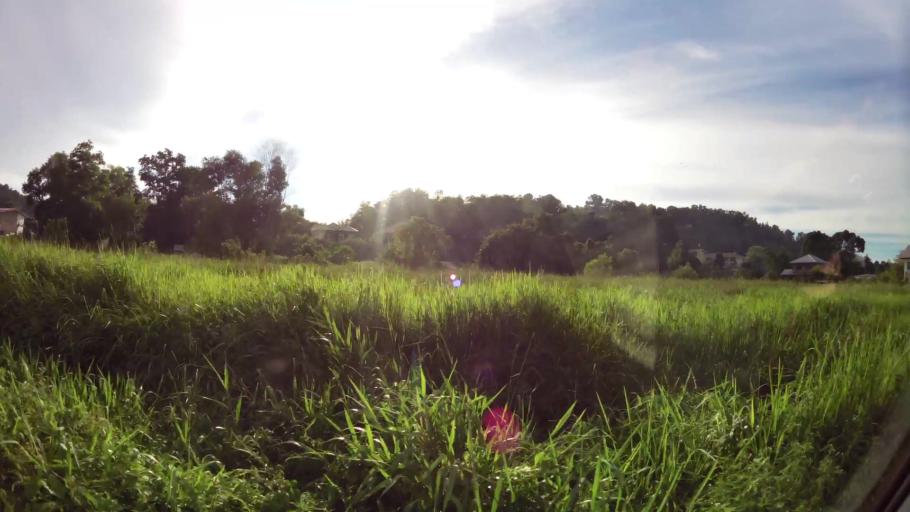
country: BN
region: Brunei and Muara
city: Bandar Seri Begawan
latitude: 4.9651
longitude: 115.0215
